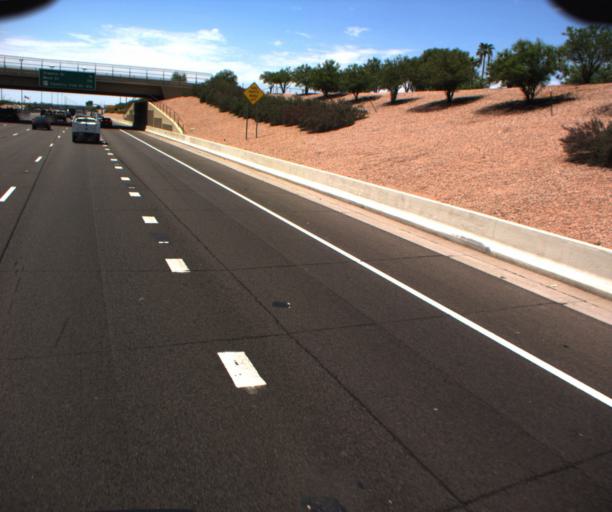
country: US
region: Arizona
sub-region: Maricopa County
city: Gilbert
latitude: 33.3864
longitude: -111.7958
